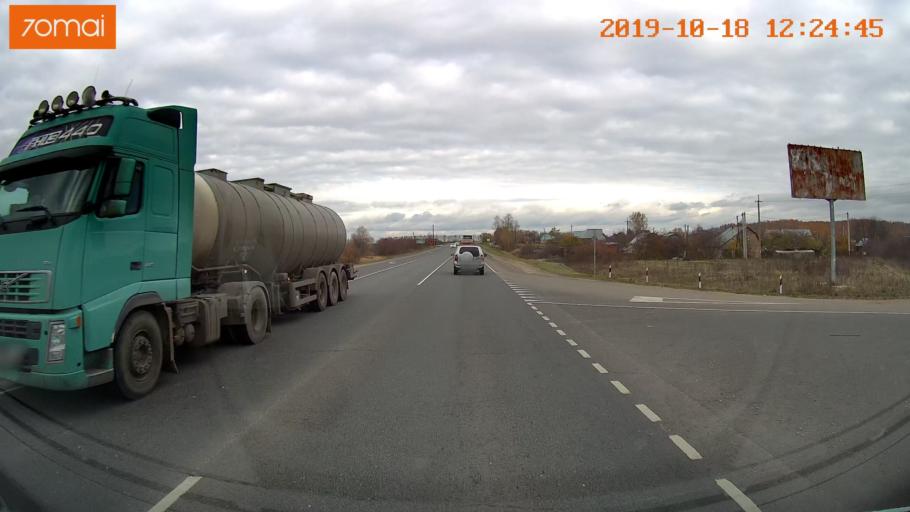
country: RU
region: Rjazan
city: Rybnoye
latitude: 54.5422
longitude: 39.5149
